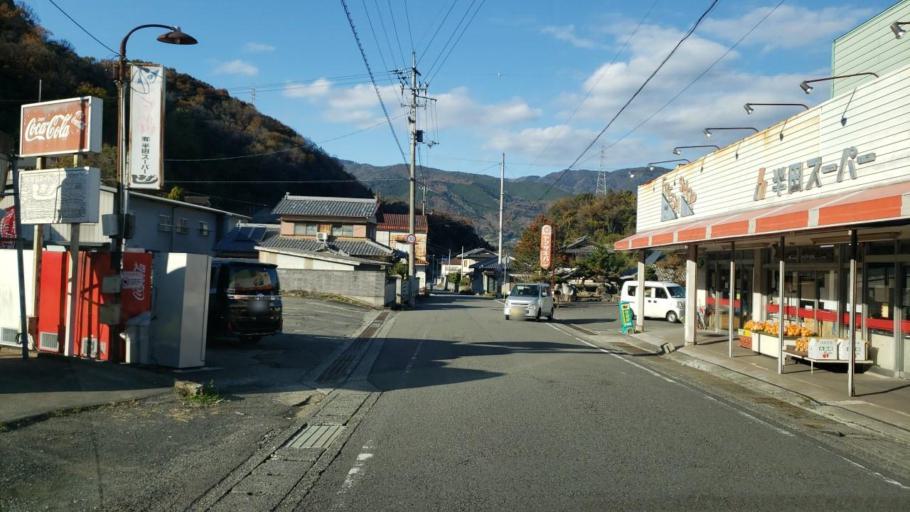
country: JP
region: Tokushima
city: Wakimachi
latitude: 34.0351
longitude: 134.0287
